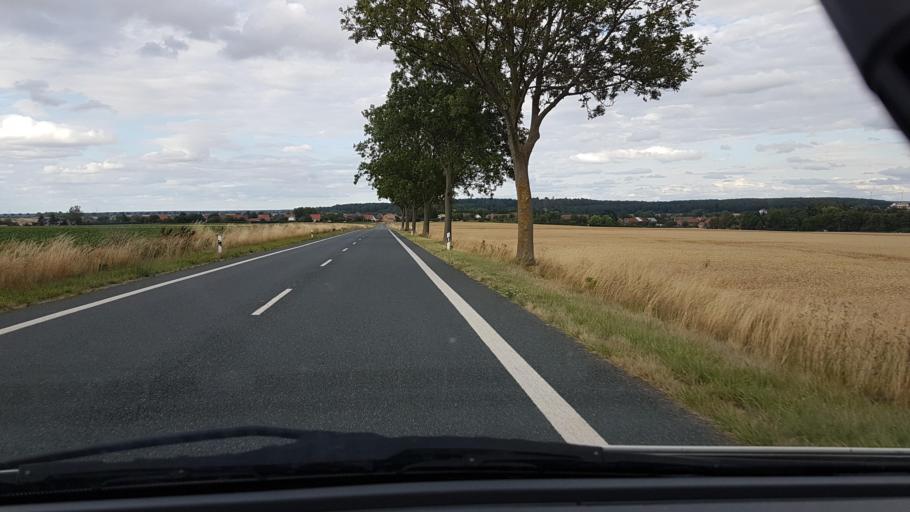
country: DE
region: Lower Saxony
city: Frellstedt
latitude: 52.2025
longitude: 10.9020
